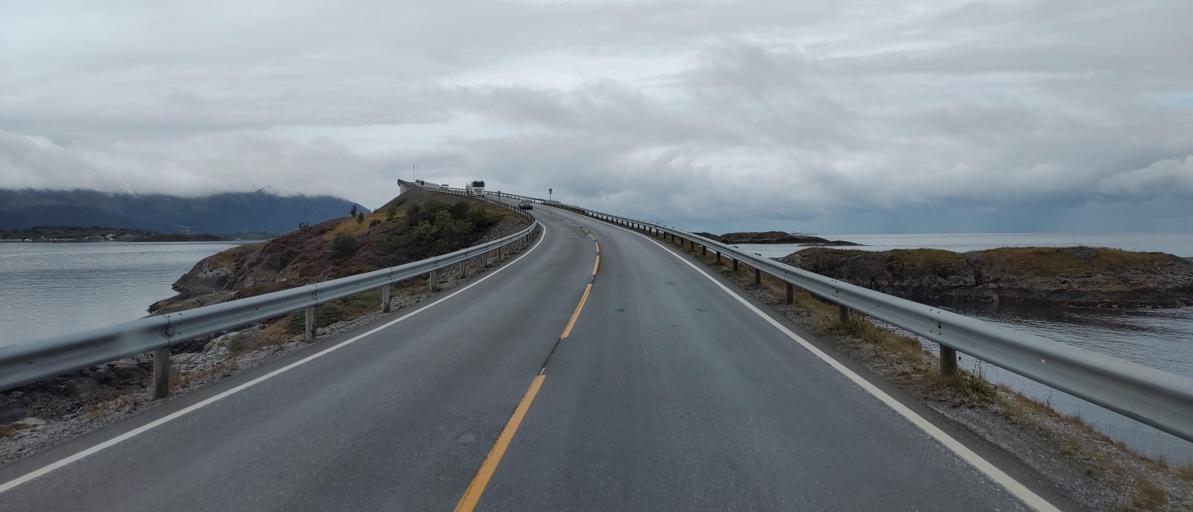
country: NO
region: More og Romsdal
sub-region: Eide
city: Eide
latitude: 63.0177
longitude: 7.3623
